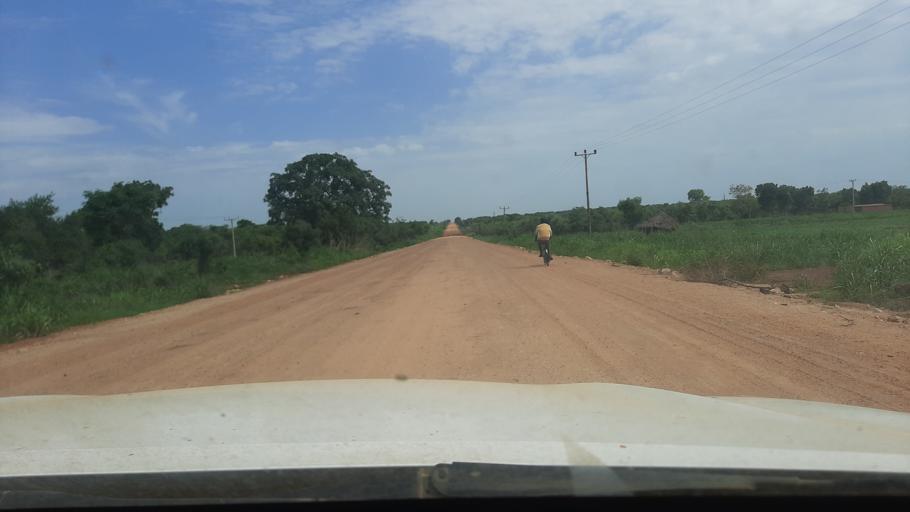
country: ET
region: Gambela
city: Gambela
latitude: 8.0235
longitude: 34.5742
